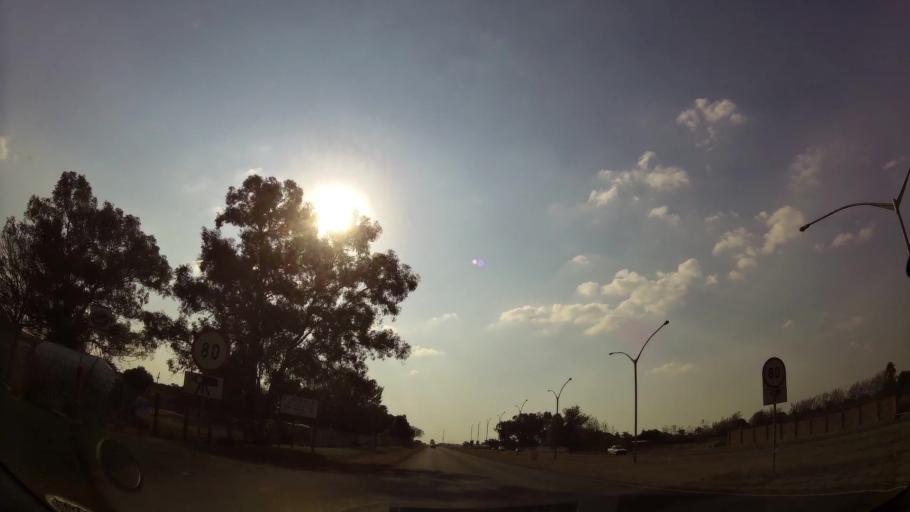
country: ZA
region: Gauteng
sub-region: Ekurhuleni Metropolitan Municipality
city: Benoni
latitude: -26.1319
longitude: 28.2901
